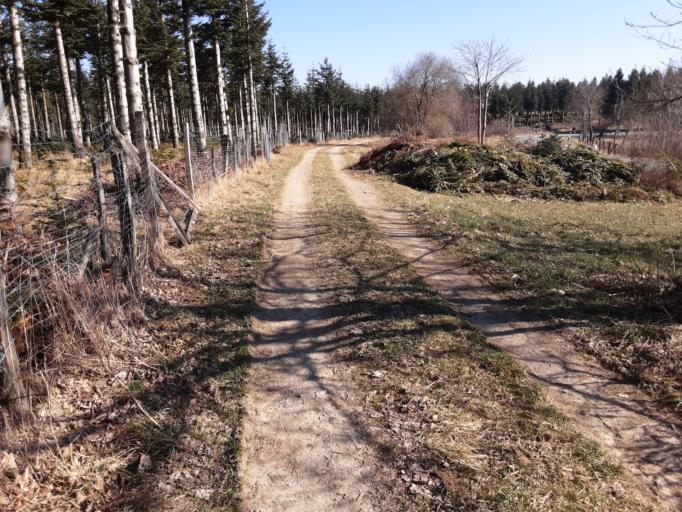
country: DE
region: North Rhine-Westphalia
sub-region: Regierungsbezirk Arnsberg
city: Winterberg
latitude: 51.1971
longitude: 8.4689
